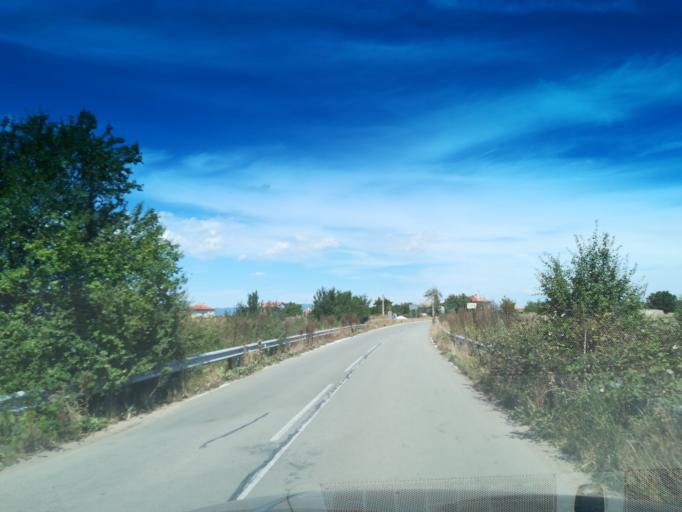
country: BG
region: Plovdiv
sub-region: Obshtina Suedinenie
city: Suedinenie
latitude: 42.4229
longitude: 24.5246
